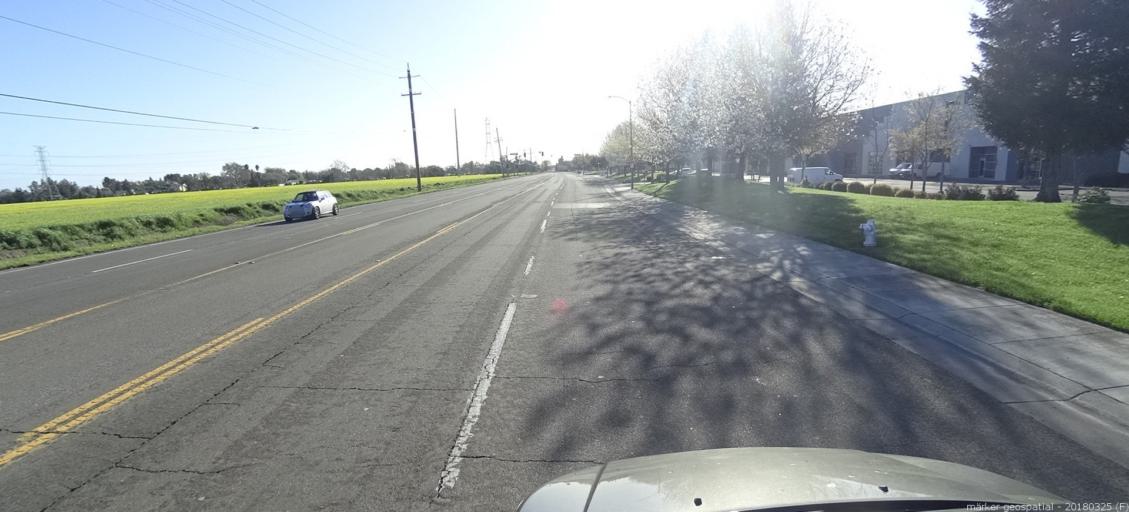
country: US
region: California
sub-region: Sacramento County
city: Rio Linda
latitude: 38.6563
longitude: -121.4898
